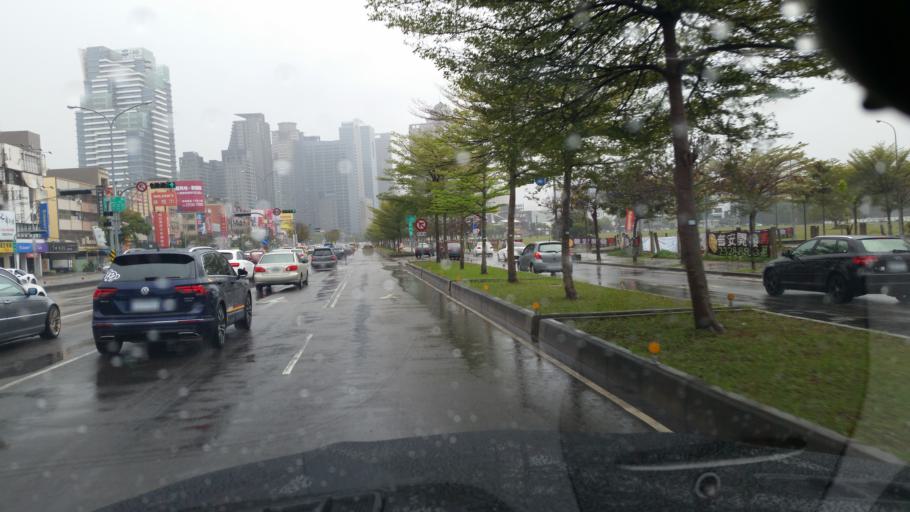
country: TW
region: Taiwan
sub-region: Taichung City
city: Taichung
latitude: 24.1625
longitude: 120.6301
